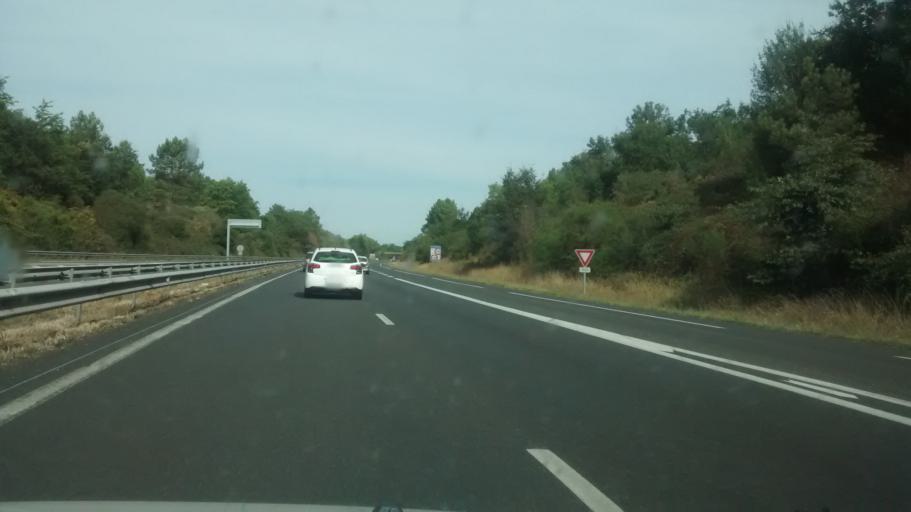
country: FR
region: Aquitaine
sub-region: Departement de la Gironde
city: Gironde-sur-Dropt
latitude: 44.5204
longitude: -0.0836
